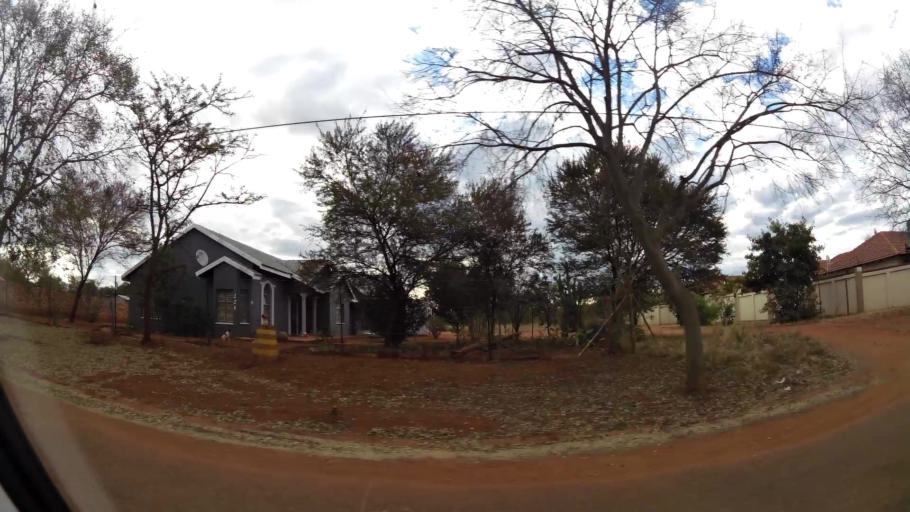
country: ZA
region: Limpopo
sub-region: Waterberg District Municipality
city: Modimolle
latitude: -24.5063
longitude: 28.7156
